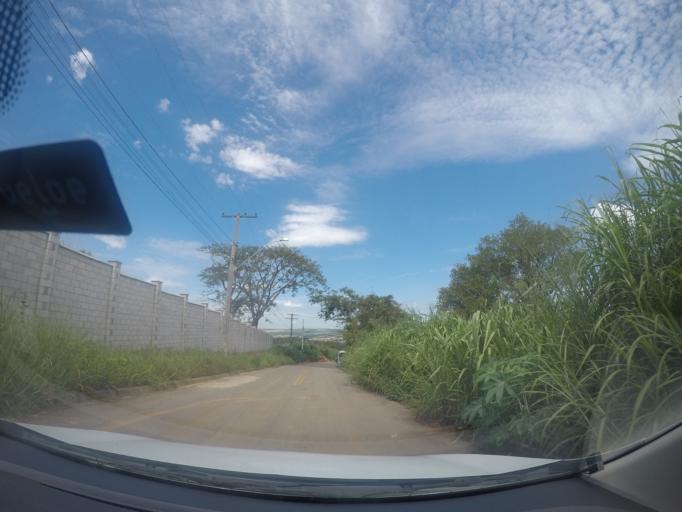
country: BR
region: Goias
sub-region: Goiania
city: Goiania
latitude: -16.6655
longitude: -49.3469
